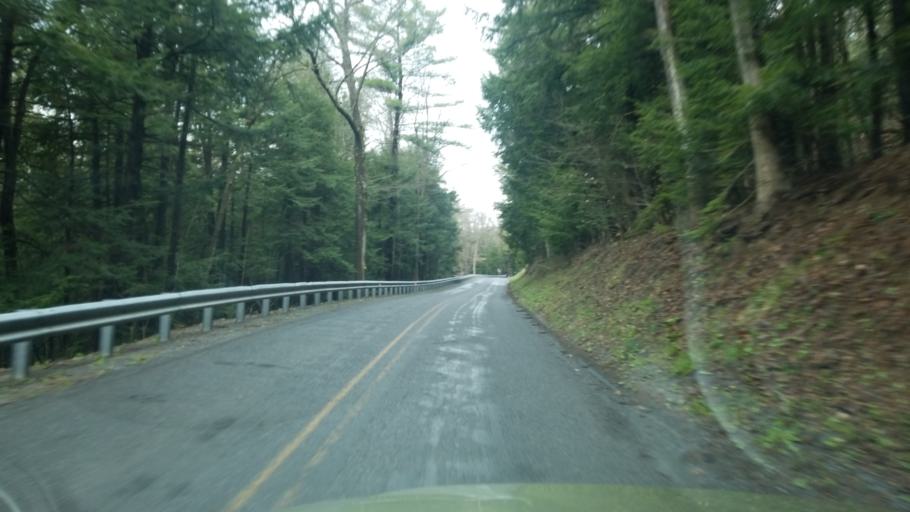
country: US
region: Pennsylvania
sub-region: Clearfield County
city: Clearfield
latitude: 41.0659
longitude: -78.4197
